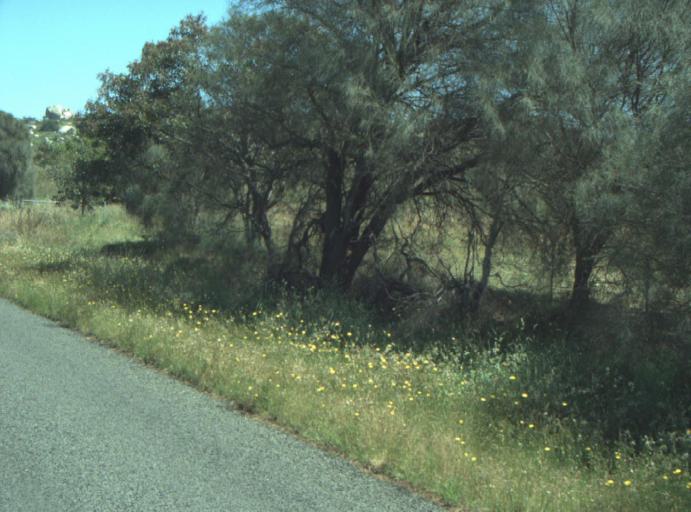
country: AU
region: Victoria
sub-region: Greater Geelong
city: Lara
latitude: -37.8784
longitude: 144.3170
